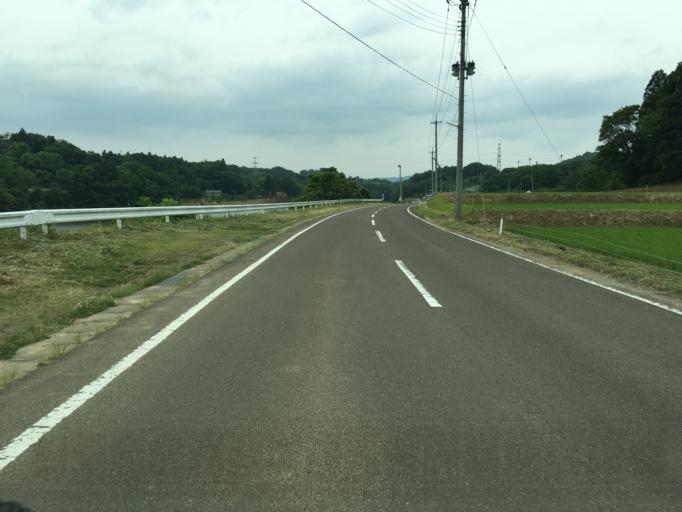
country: JP
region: Fukushima
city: Nihommatsu
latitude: 37.6261
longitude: 140.5232
